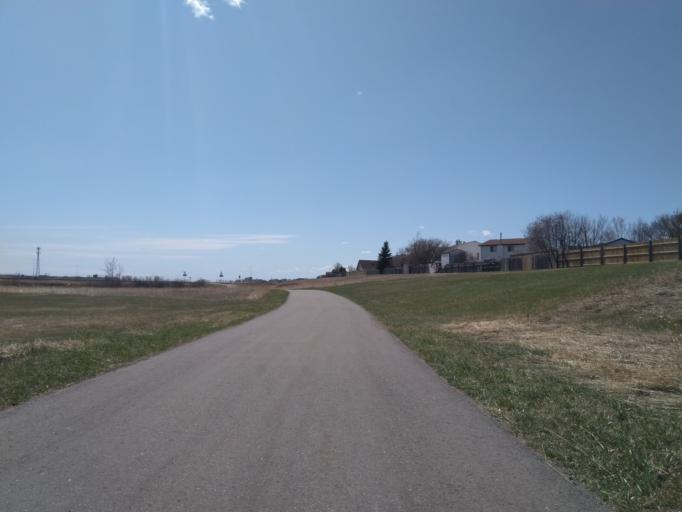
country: CA
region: Alberta
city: Chestermere
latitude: 51.0568
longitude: -113.9232
